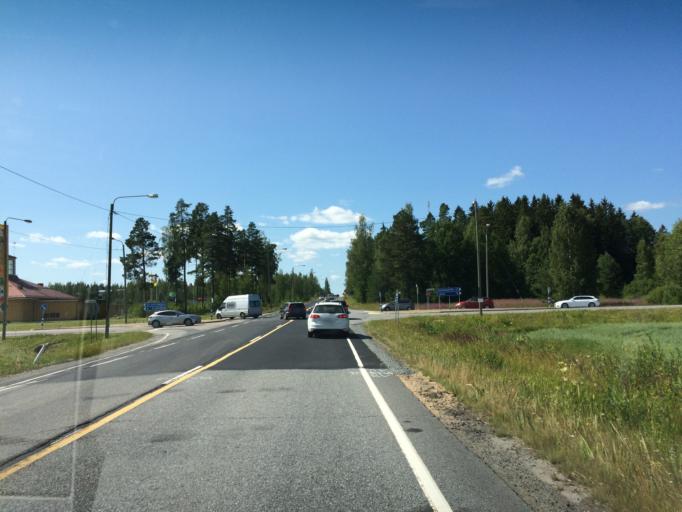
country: FI
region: Pirkanmaa
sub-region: Lounais-Pirkanmaa
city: Kiikoinen
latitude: 61.4753
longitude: 22.5589
